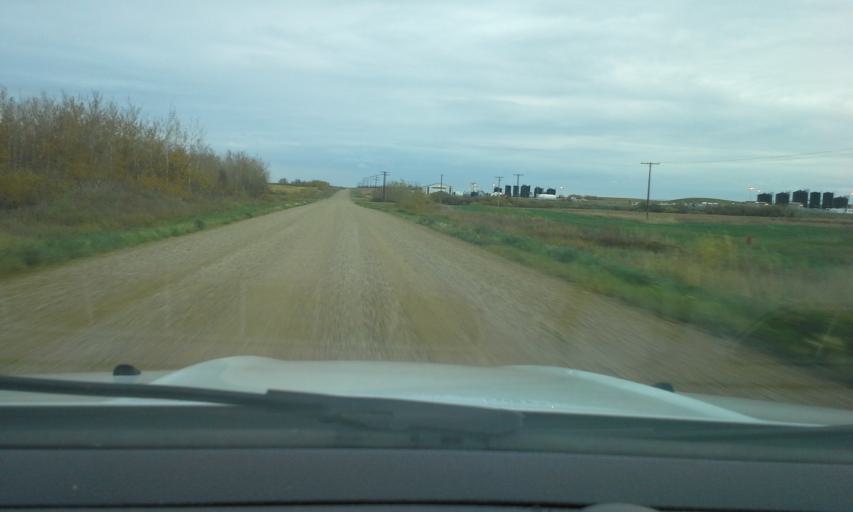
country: CA
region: Saskatchewan
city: Lloydminster
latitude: 53.2902
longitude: -109.8084
